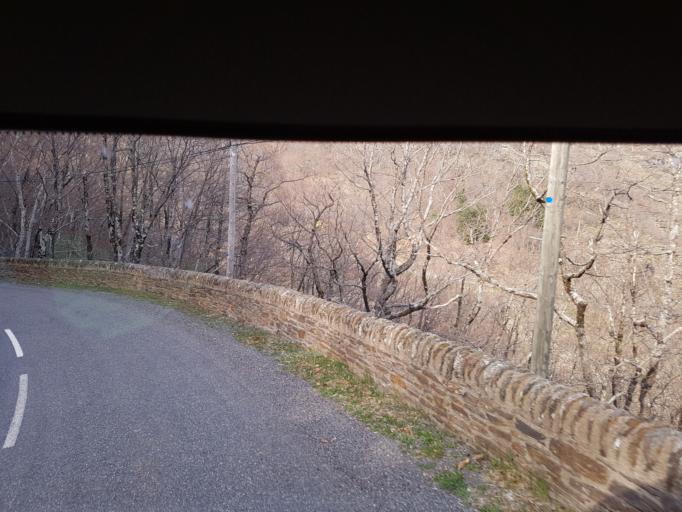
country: FR
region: Languedoc-Roussillon
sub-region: Departement du Gard
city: Branoux-les-Taillades
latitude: 44.3271
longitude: 3.8407
